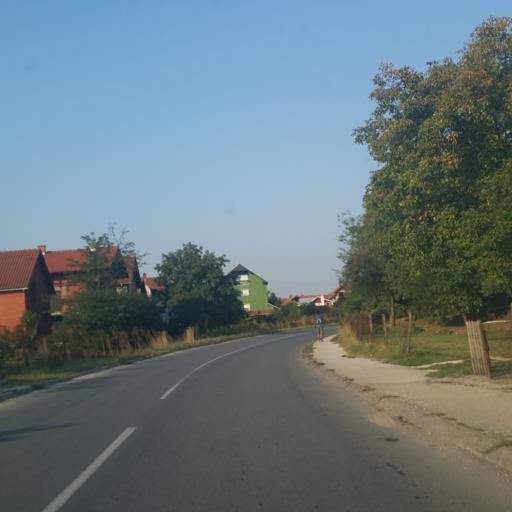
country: RS
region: Central Serbia
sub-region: Zajecarski Okrug
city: Zajecar
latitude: 43.9127
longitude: 22.2701
